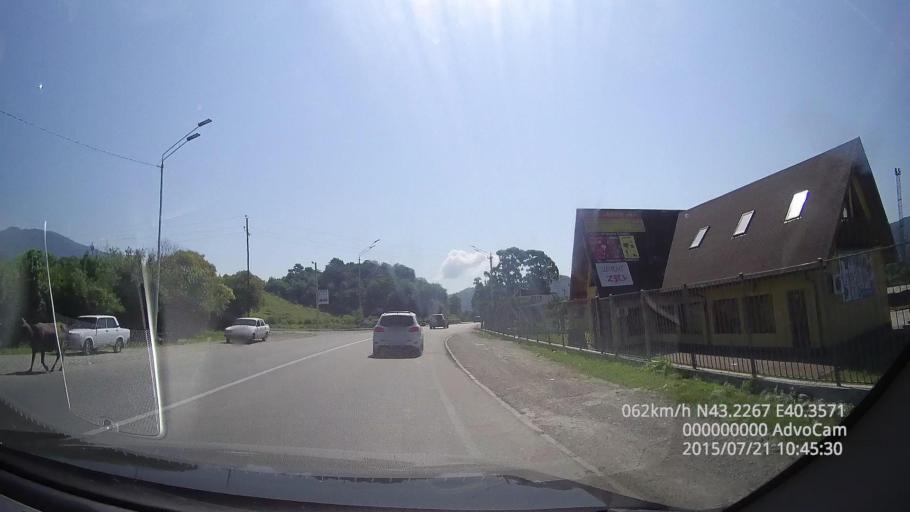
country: GE
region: Abkhazia
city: Bich'vinta
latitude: 43.2267
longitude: 40.3574
